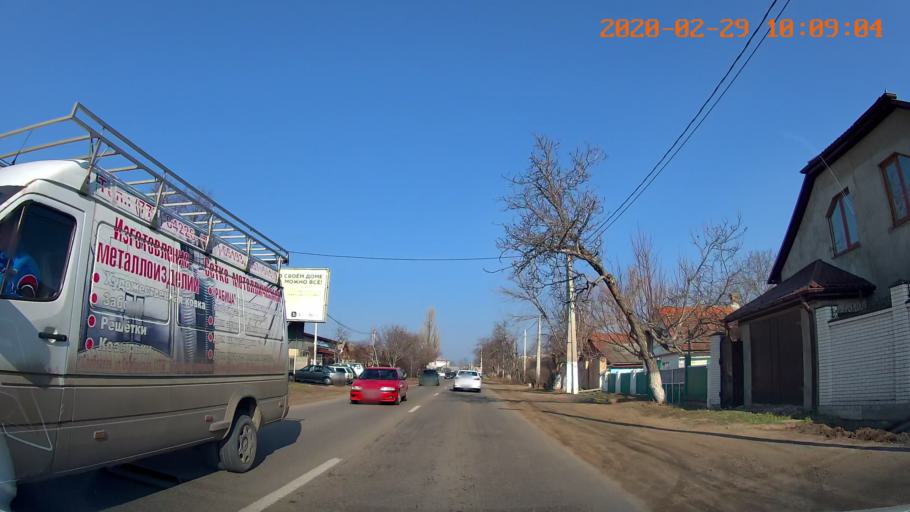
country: MD
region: Telenesti
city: Tiraspolul Nou
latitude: 46.8261
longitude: 29.6545
